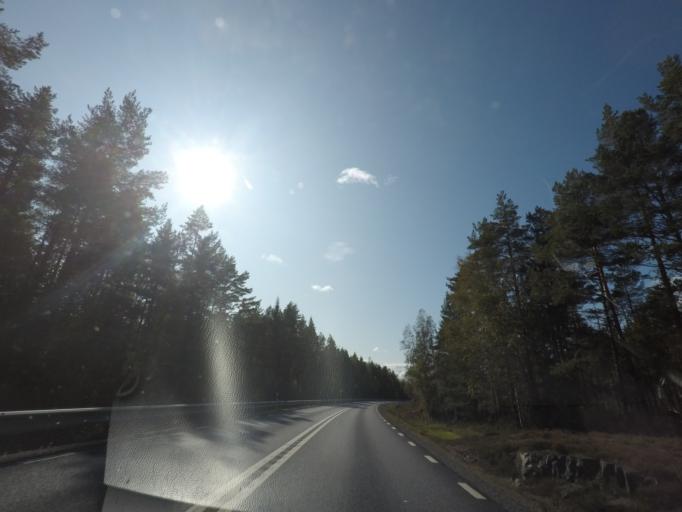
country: SE
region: Vaestmanland
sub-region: Skinnskattebergs Kommun
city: Skinnskatteberg
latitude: 59.8348
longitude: 15.5576
